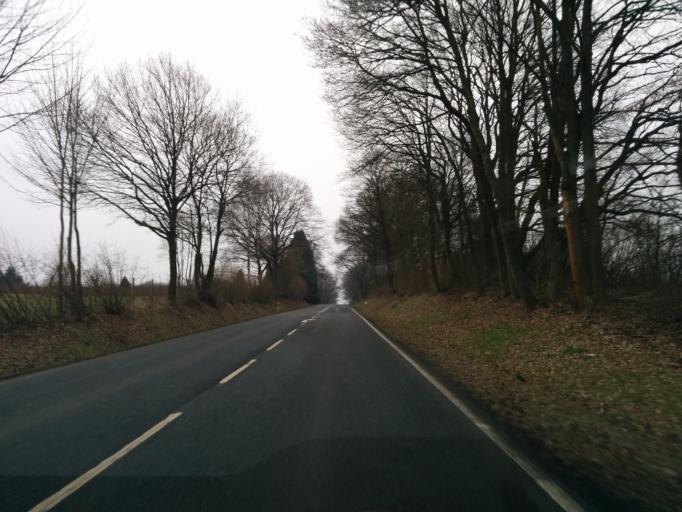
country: DE
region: Rheinland-Pfalz
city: Eitelborn
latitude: 50.3651
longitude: 7.6992
